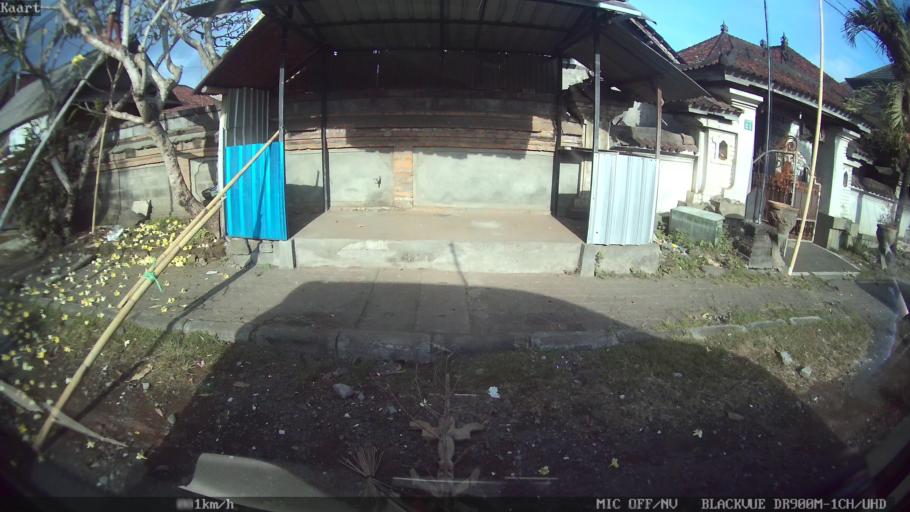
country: ID
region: Bali
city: Banjar Parekan
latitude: -8.5777
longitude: 115.2176
